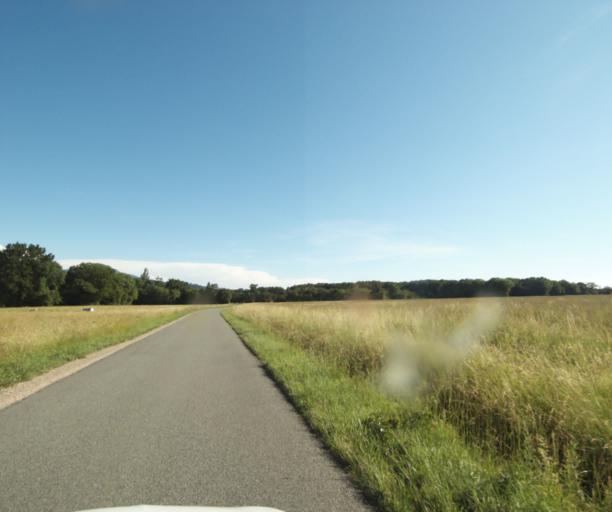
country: FR
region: Rhone-Alpes
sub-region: Departement de la Haute-Savoie
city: Massongy
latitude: 46.3420
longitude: 6.3284
